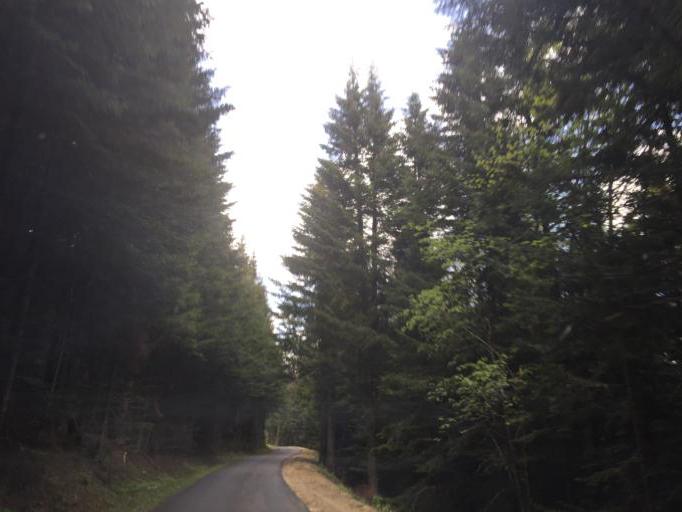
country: FR
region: Rhone-Alpes
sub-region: Departement de la Loire
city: Saint-Sauveur-en-Rue
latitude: 45.2786
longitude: 4.4733
